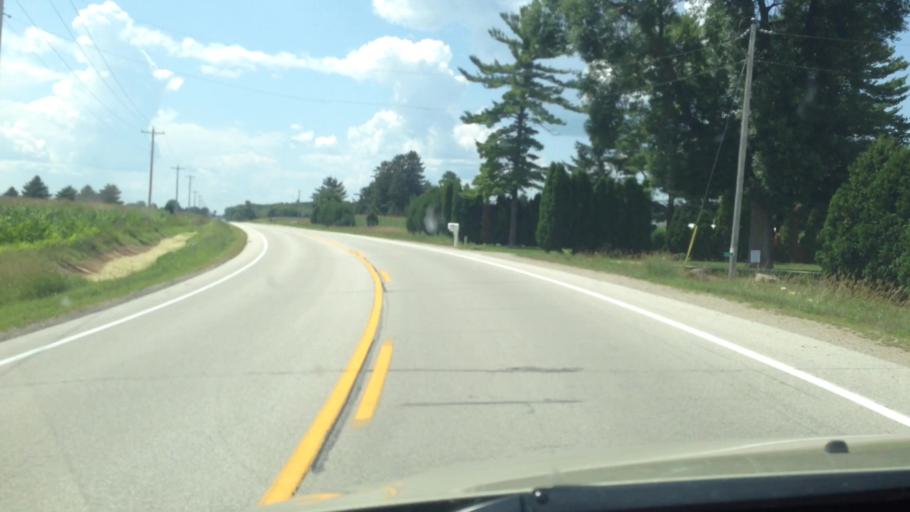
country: US
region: Wisconsin
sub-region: Brown County
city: Pulaski
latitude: 44.6590
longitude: -88.1833
